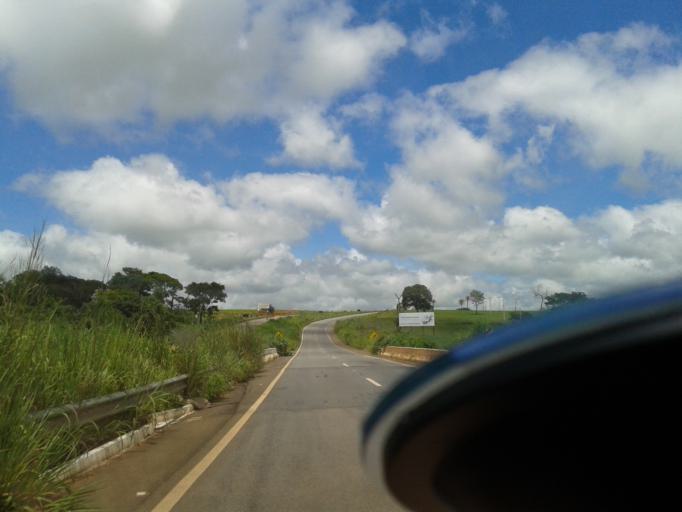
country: BR
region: Goias
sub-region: Itaberai
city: Itaberai
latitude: -16.0970
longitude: -49.7055
